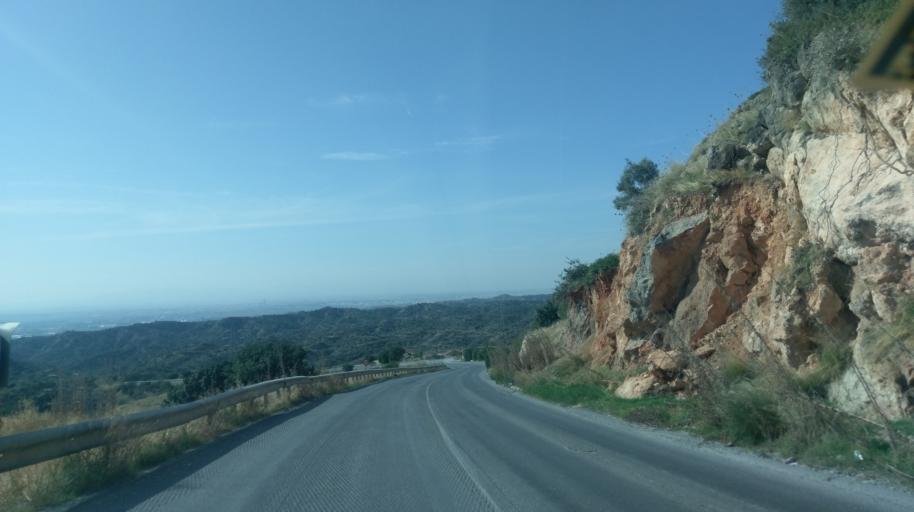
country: CY
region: Lefkosia
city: Nicosia
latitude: 35.2661
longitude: 33.4611
